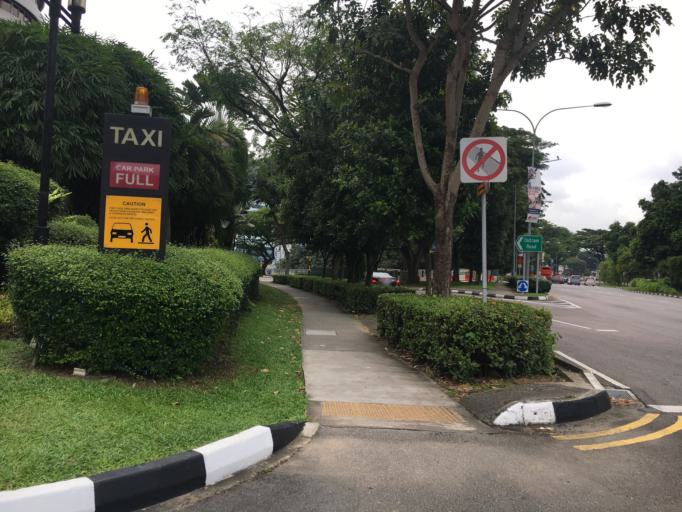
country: SG
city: Singapore
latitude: 1.2887
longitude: 103.8370
